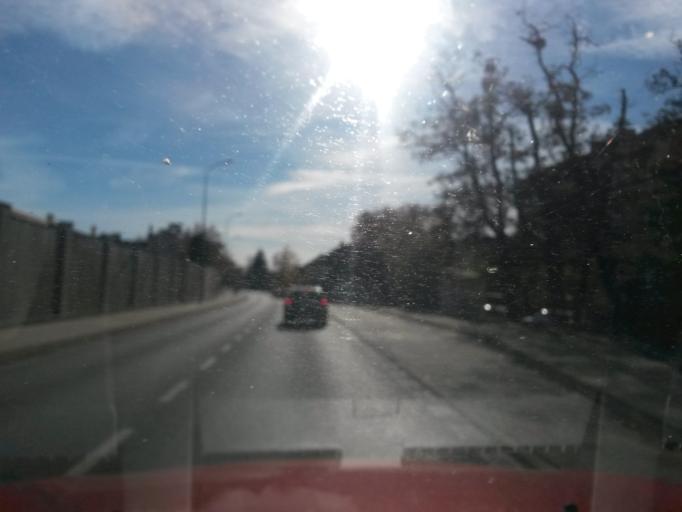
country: SK
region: Presovsky
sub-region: Okres Presov
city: Presov
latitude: 48.9976
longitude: 21.2358
